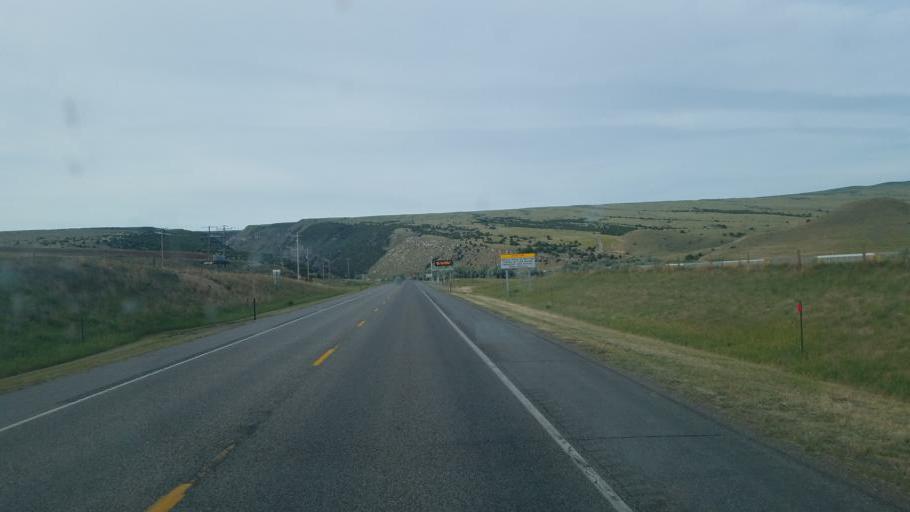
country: US
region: Wyoming
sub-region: Hot Springs County
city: Thermopolis
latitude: 43.5879
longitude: -108.2132
